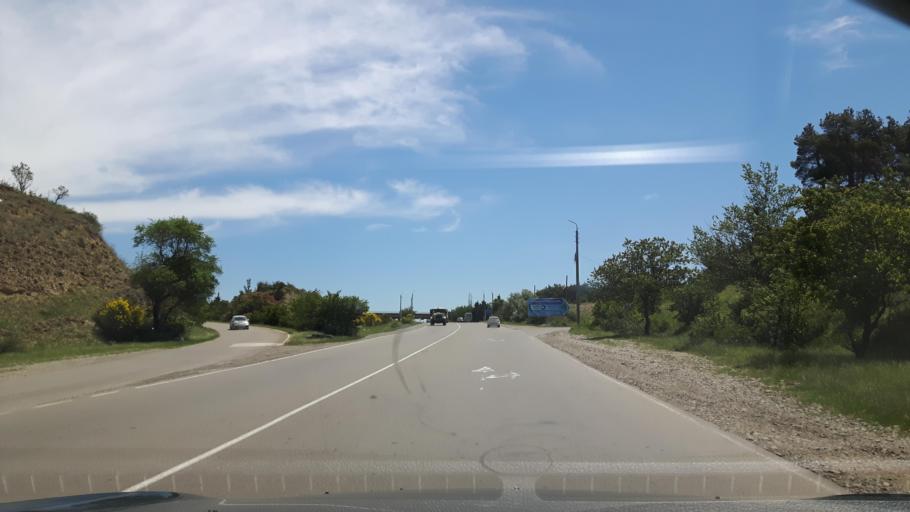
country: GE
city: Didi Lilo
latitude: 41.6886
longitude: 45.0163
